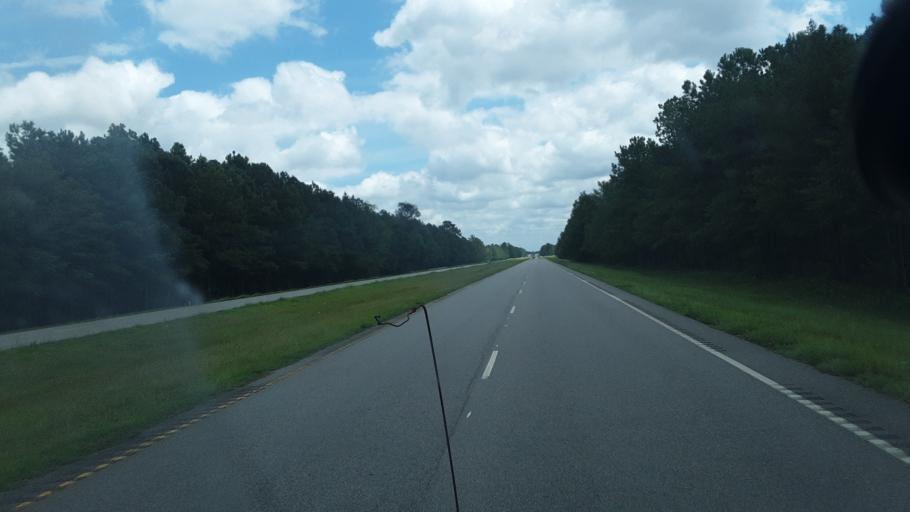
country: US
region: South Carolina
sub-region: Horry County
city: Loris
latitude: 34.0914
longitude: -78.9017
